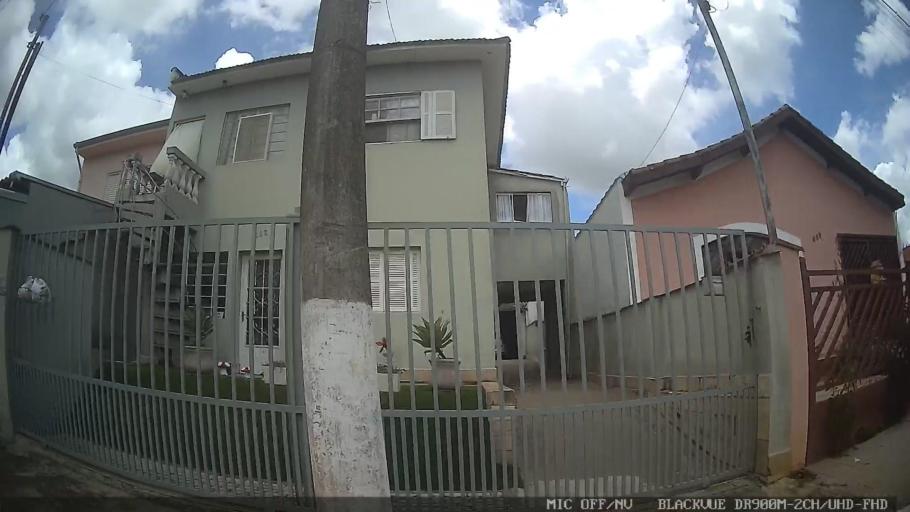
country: BR
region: Sao Paulo
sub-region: Amparo
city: Amparo
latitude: -22.8120
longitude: -46.6953
